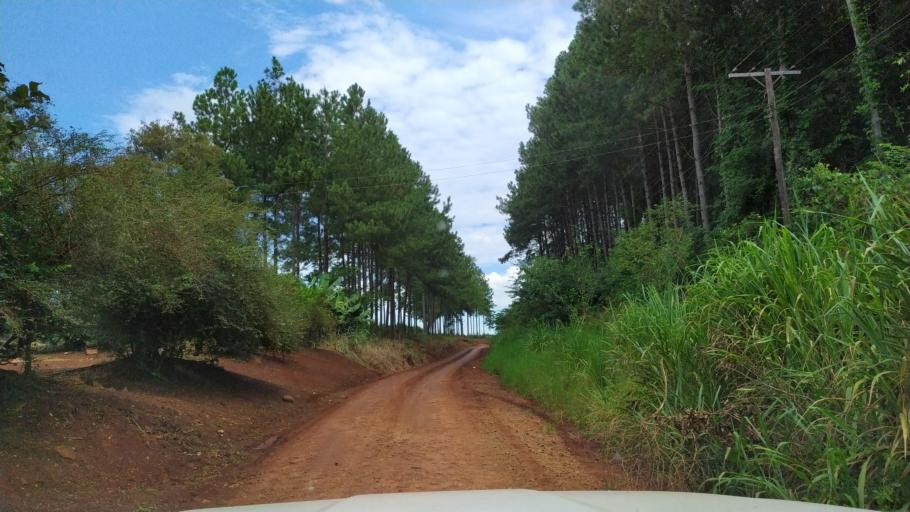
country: AR
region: Misiones
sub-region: Departamento de Eldorado
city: Eldorado
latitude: -26.5260
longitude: -54.5973
